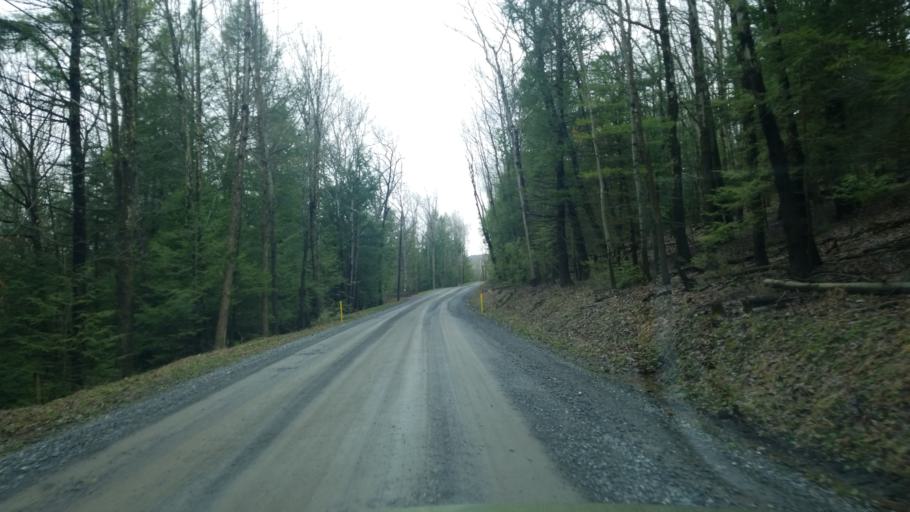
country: US
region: Pennsylvania
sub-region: Clearfield County
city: Shiloh
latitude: 41.1180
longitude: -78.3413
